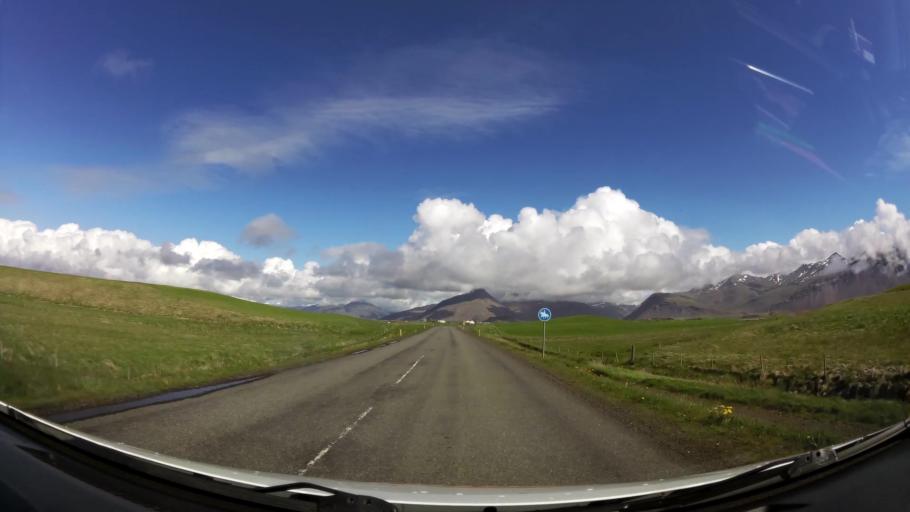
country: IS
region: East
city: Hoefn
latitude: 64.2680
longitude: -15.2019
